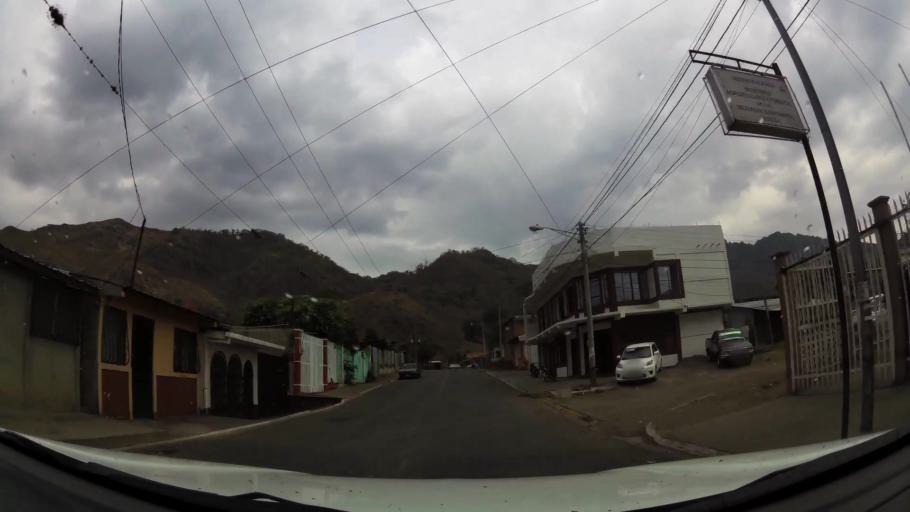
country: NI
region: Jinotega
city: Jinotega
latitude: 13.0912
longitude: -85.9964
